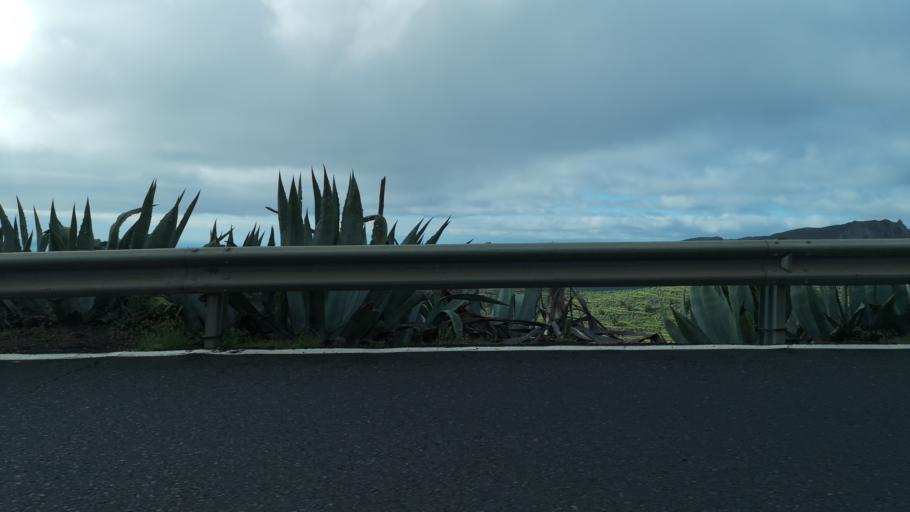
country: ES
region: Canary Islands
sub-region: Provincia de Santa Cruz de Tenerife
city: San Sebastian de la Gomera
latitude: 28.0954
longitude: -17.1593
